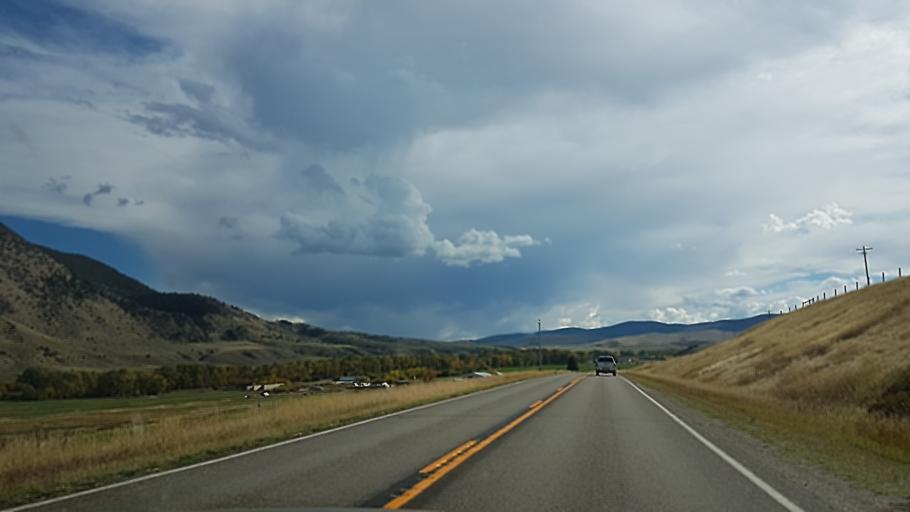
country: US
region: Montana
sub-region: Jefferson County
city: Whitehall
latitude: 45.8253
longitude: -111.9339
